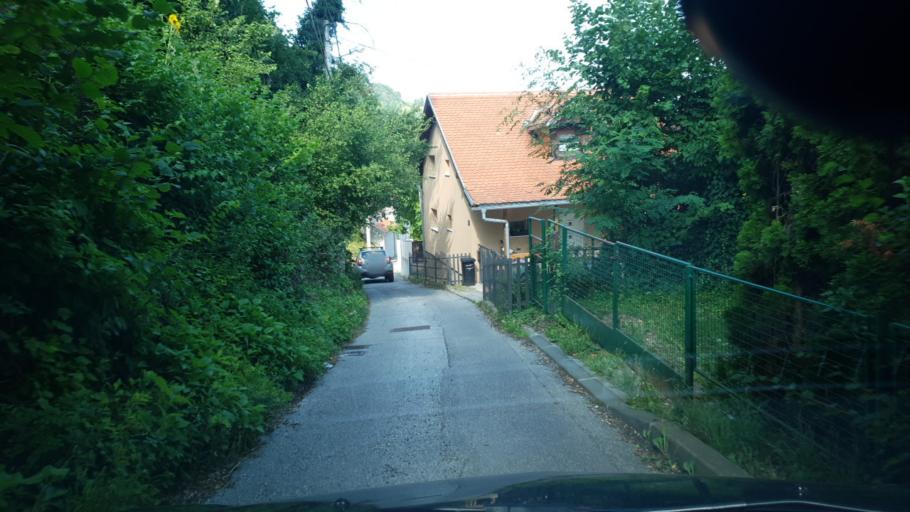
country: HR
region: Grad Zagreb
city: Zagreb
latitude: 45.8590
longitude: 15.9682
